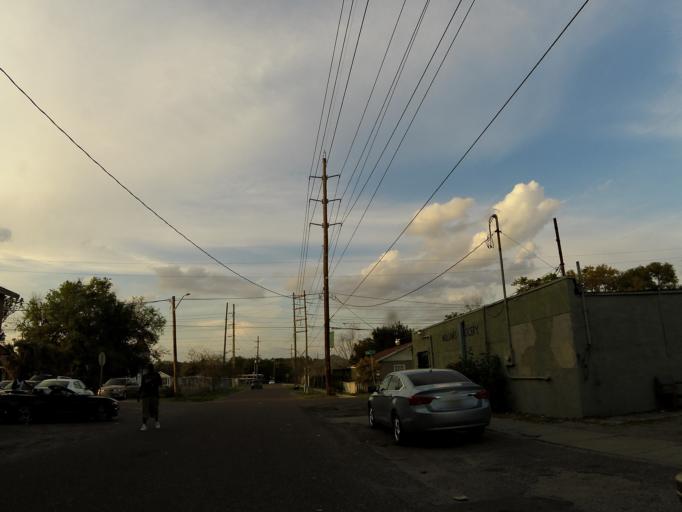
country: US
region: Florida
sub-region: Duval County
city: Jacksonville
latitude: 30.3616
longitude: -81.6328
